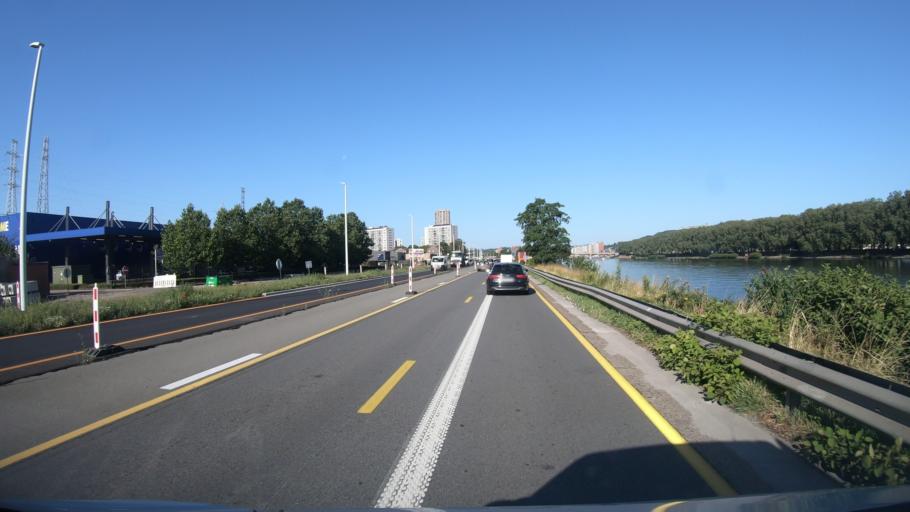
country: BE
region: Wallonia
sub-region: Province de Liege
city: Herstal
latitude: 50.6527
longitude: 5.6114
